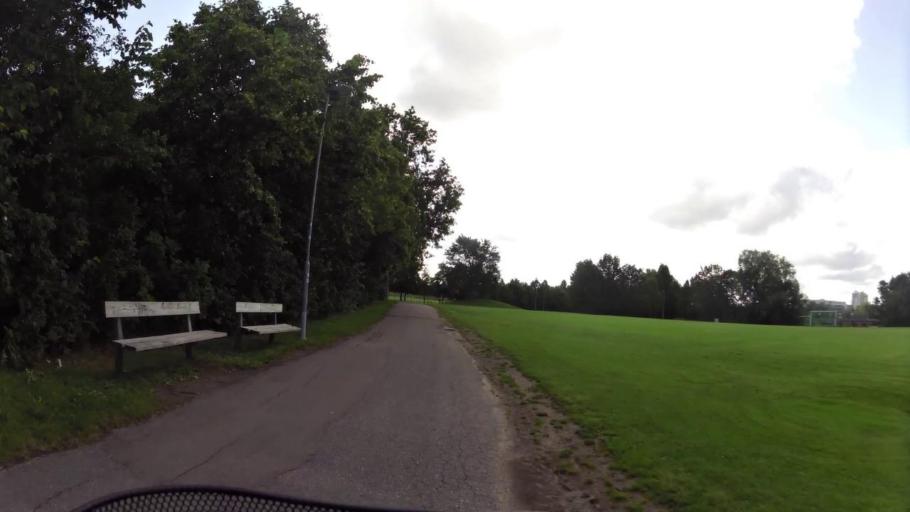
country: SE
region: OEstergoetland
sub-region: Linkopings Kommun
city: Linkoping
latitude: 58.4170
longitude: 15.6312
